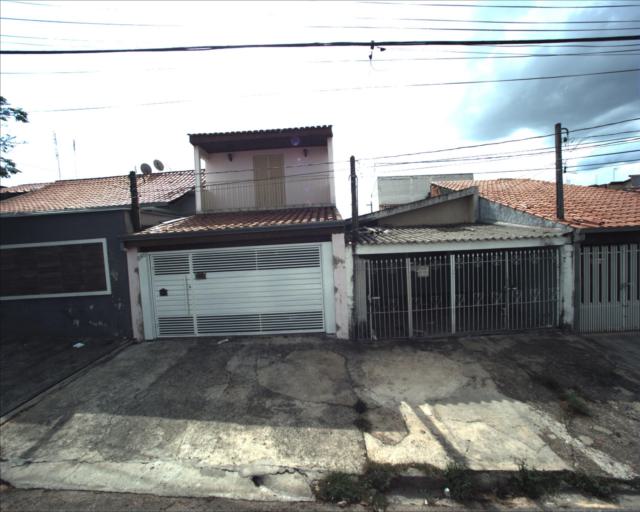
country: BR
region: Sao Paulo
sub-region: Sorocaba
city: Sorocaba
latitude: -23.4648
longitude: -47.4719
